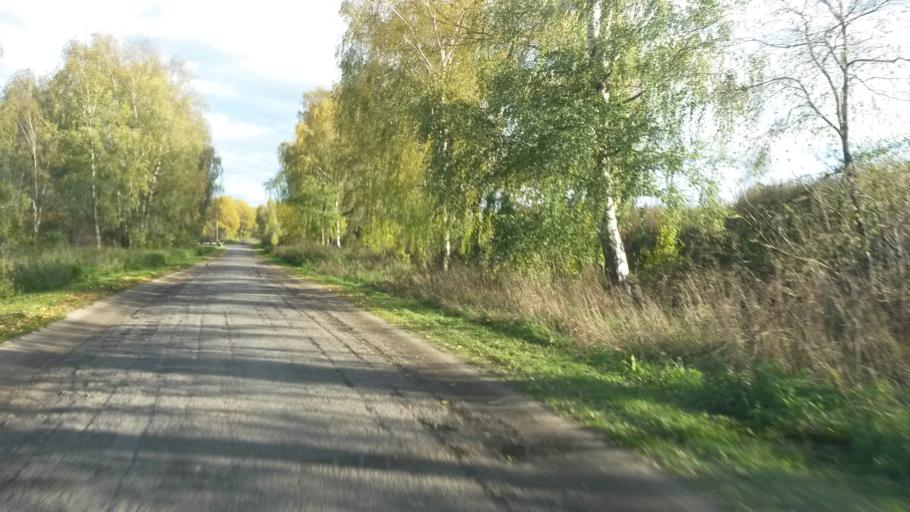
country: RU
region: Jaroslavl
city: Tunoshna
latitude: 57.5250
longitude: 40.0070
